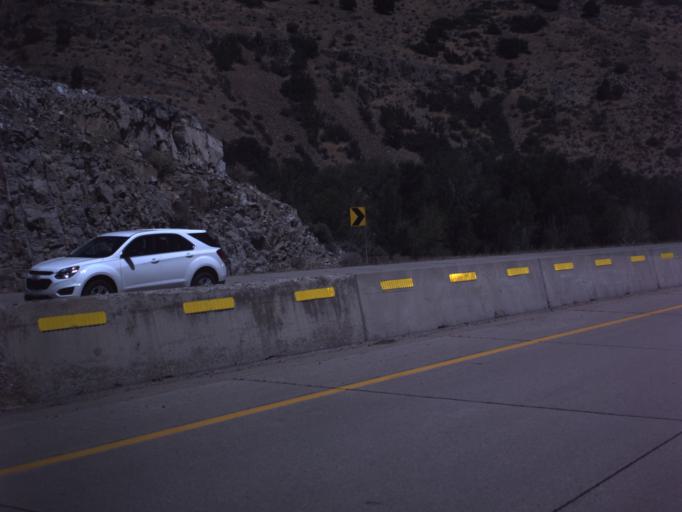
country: US
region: Utah
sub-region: Morgan County
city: Morgan
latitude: 41.0529
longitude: -111.6016
